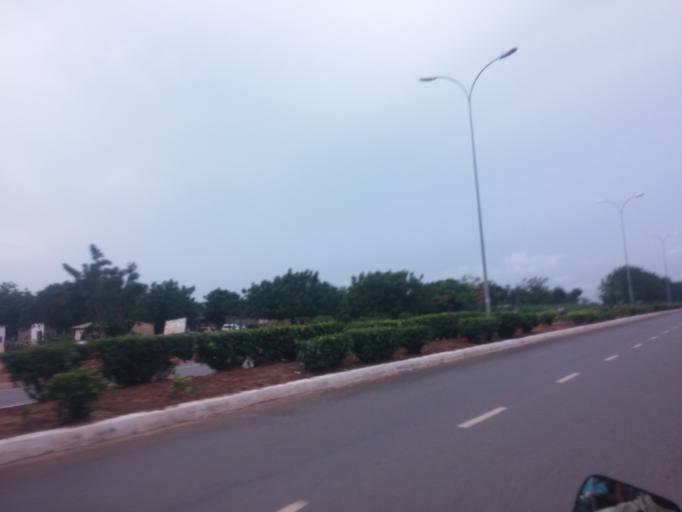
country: TG
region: Maritime
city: Lome
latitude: 6.1945
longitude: 1.2105
